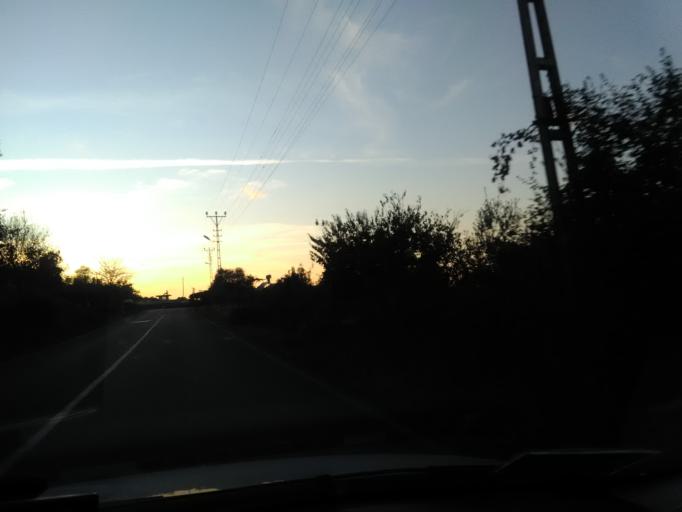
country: TR
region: Antalya
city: Gazipasa
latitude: 36.2597
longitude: 32.3162
